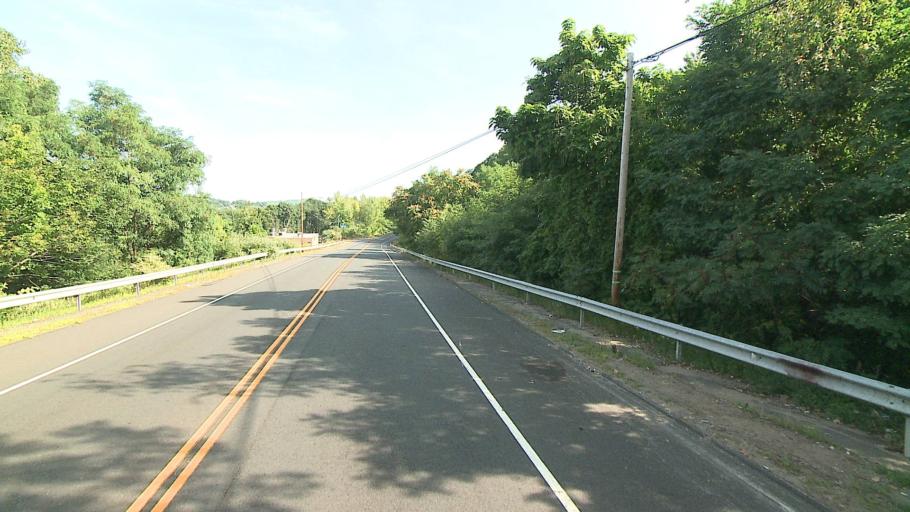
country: US
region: Connecticut
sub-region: New Haven County
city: Waterbury
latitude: 41.5683
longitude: -73.0545
